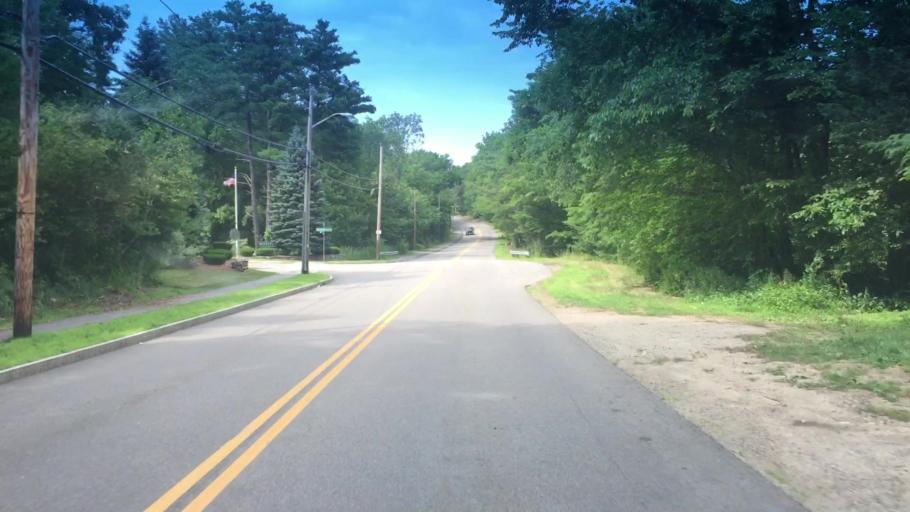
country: US
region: Massachusetts
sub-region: Norfolk County
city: Medway
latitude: 42.1145
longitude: -71.3958
